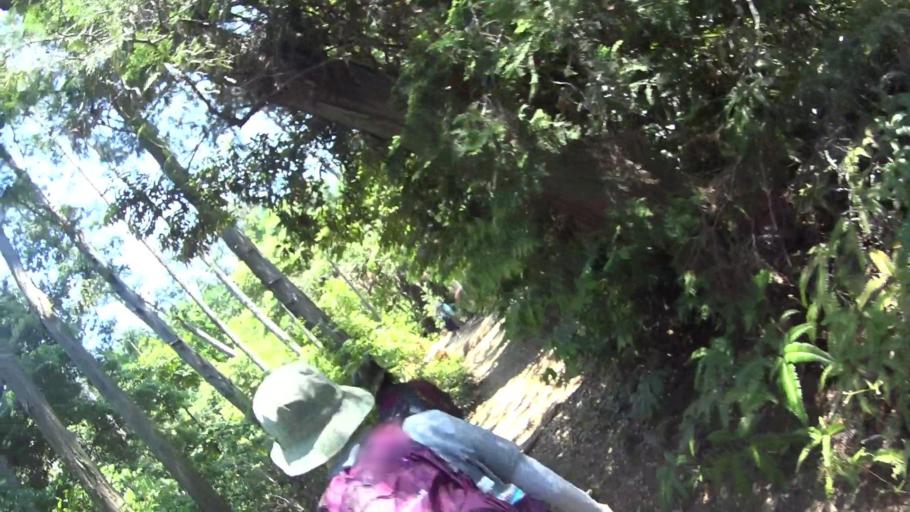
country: JP
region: Kyoto
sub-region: Kyoto-shi
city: Kamigyo-ku
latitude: 35.0099
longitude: 135.8019
